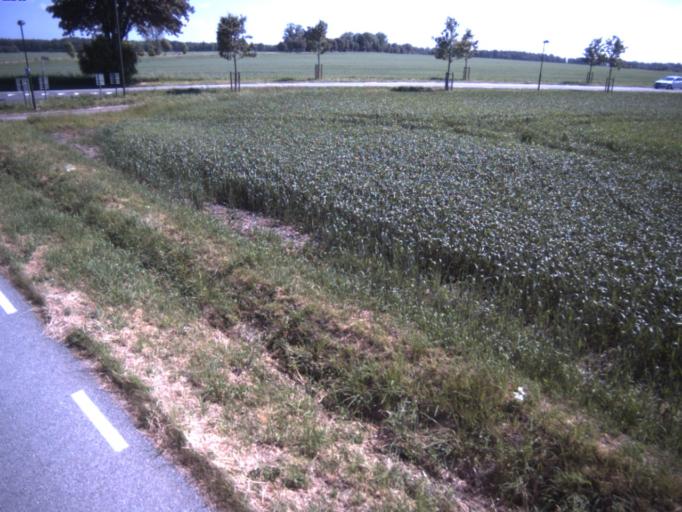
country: DK
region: Capital Region
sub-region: Helsingor Kommune
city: Helsingor
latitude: 56.1055
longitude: 12.6394
